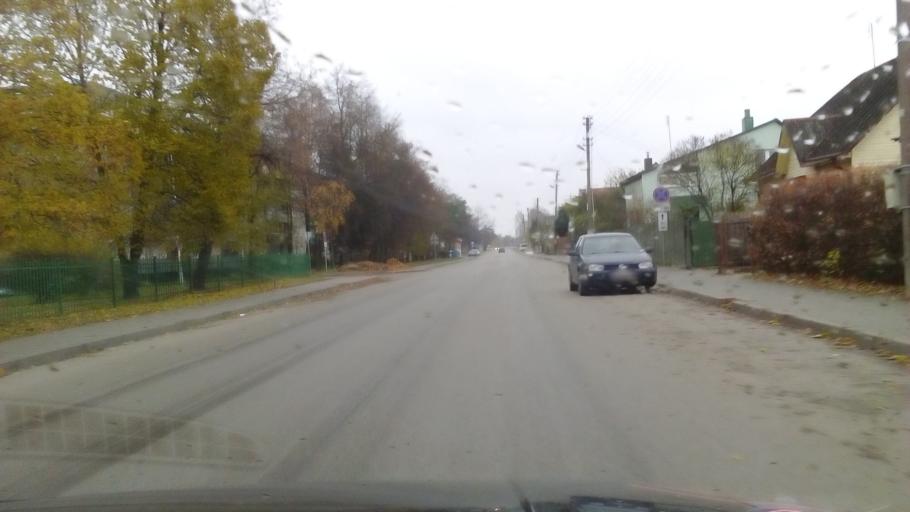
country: LT
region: Marijampoles apskritis
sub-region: Marijampole Municipality
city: Marijampole
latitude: 54.5604
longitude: 23.3580
